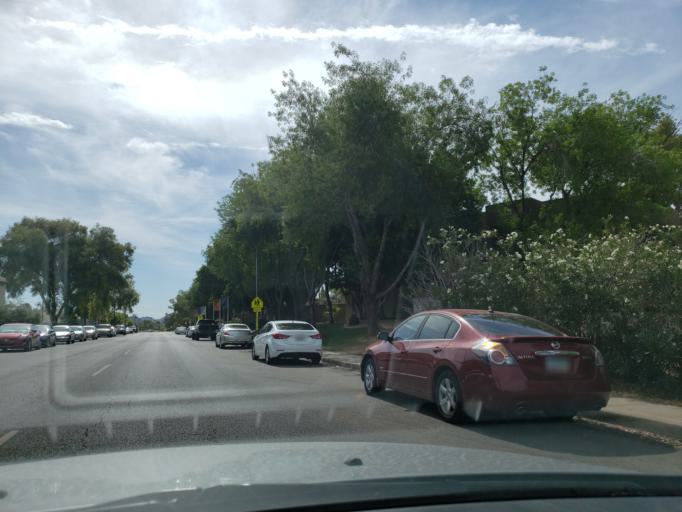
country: US
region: Arizona
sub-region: Maricopa County
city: Glendale
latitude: 33.5603
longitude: -112.1048
